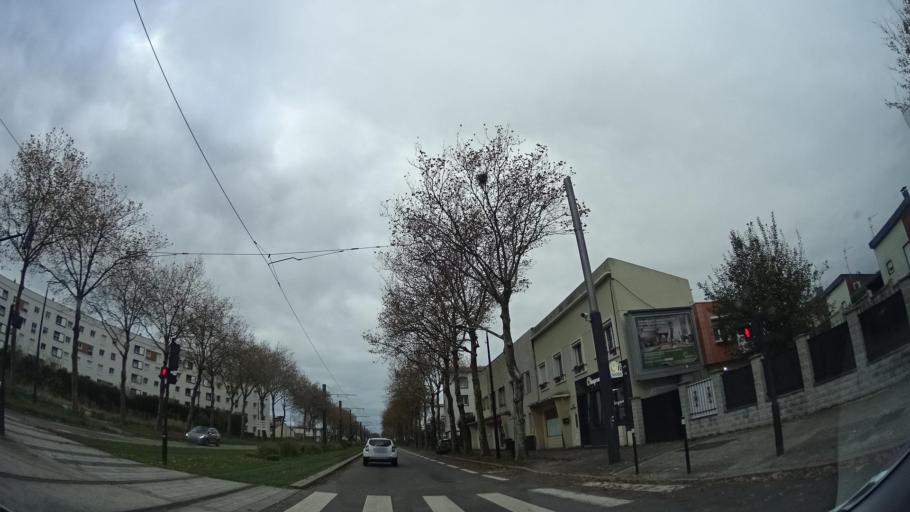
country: FR
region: Haute-Normandie
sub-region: Departement de la Seine-Maritime
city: Le Havre
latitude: 49.5130
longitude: 0.1255
